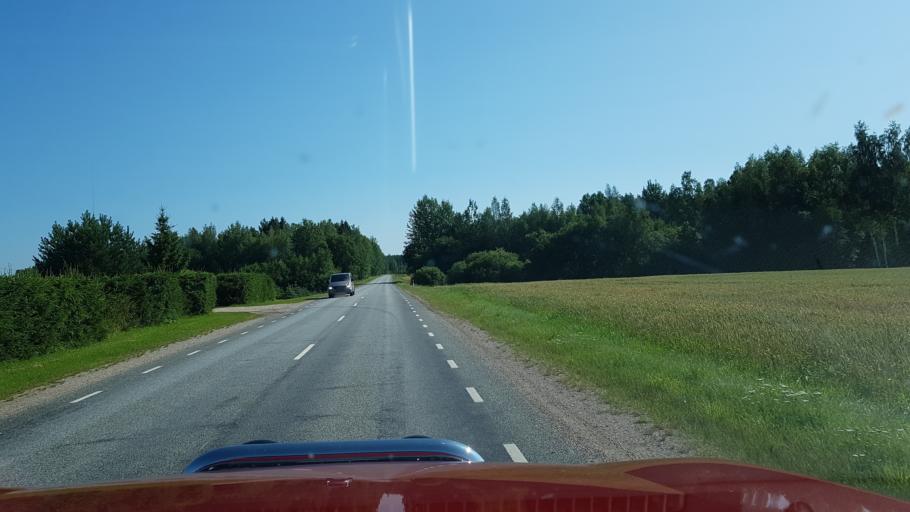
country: EE
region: Polvamaa
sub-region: Polva linn
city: Polva
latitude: 58.0018
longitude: 26.9340
